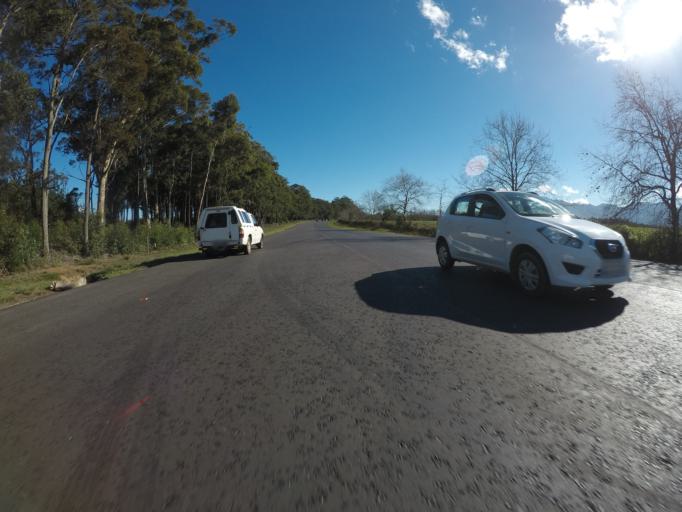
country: ZA
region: Western Cape
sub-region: Overberg District Municipality
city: Grabouw
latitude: -34.1779
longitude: 19.0651
